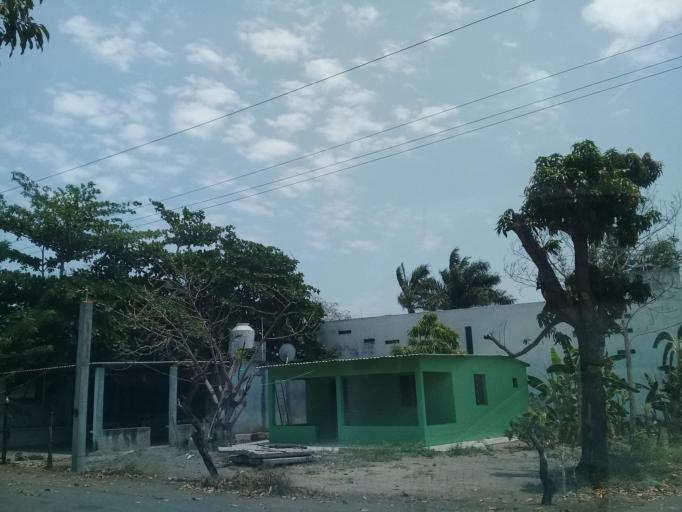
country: MX
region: Veracruz
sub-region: Veracruz
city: Delfino Victoria (Santa Fe)
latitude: 19.1706
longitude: -96.2989
